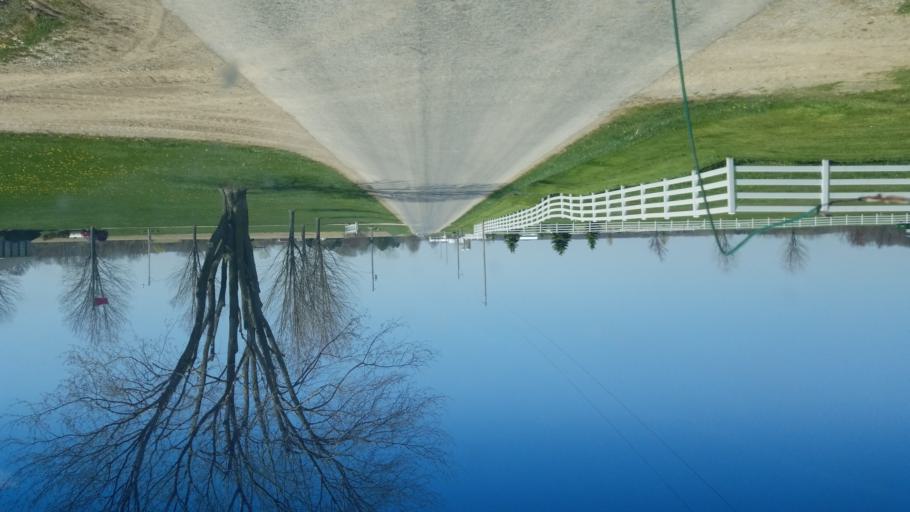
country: US
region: Ohio
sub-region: Huron County
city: Greenwich
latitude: 41.0473
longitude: -82.4722
